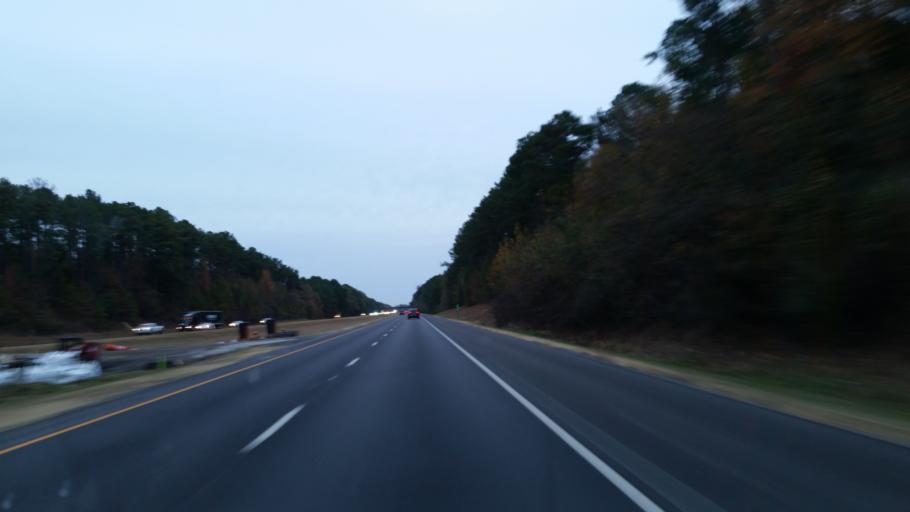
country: US
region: Alabama
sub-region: Greene County
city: Eutaw
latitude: 32.8238
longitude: -87.9876
